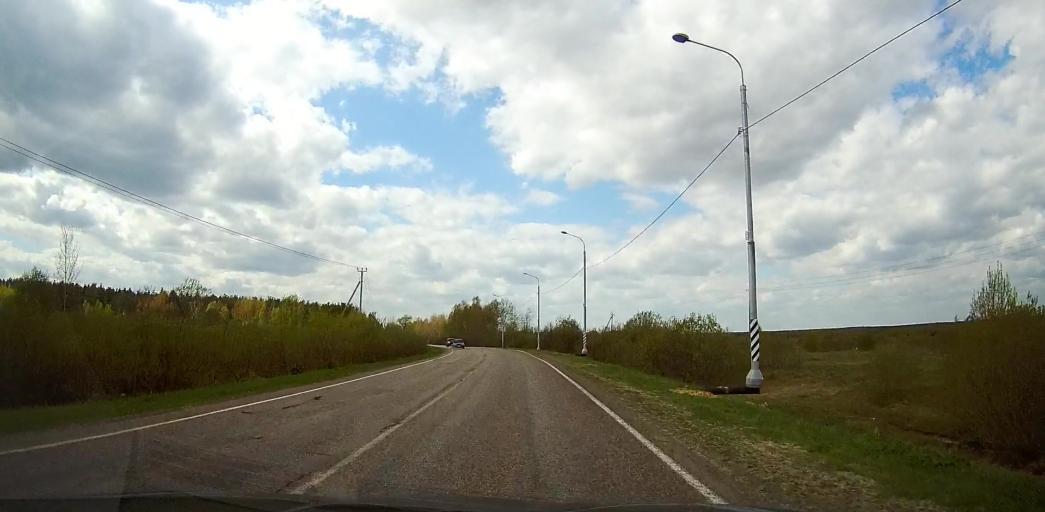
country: RU
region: Moskovskaya
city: Davydovo
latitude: 55.6654
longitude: 38.7982
